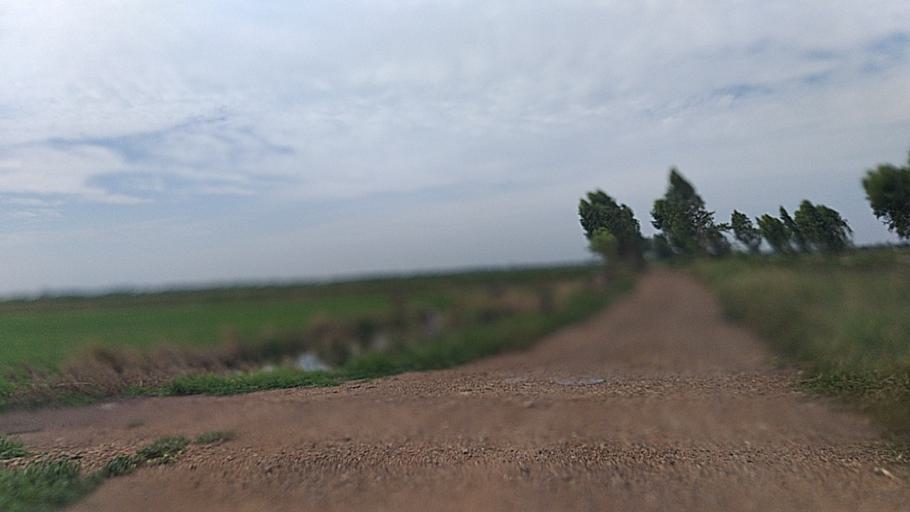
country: TH
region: Pathum Thani
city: Ban Lam Luk Ka
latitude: 14.0281
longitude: 100.8565
